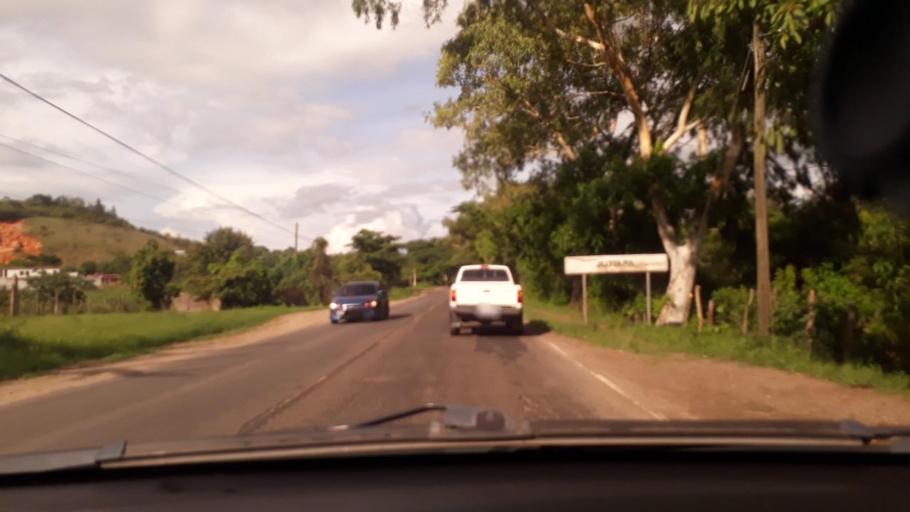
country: GT
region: Jutiapa
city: Jutiapa
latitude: 14.2899
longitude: -89.9296
